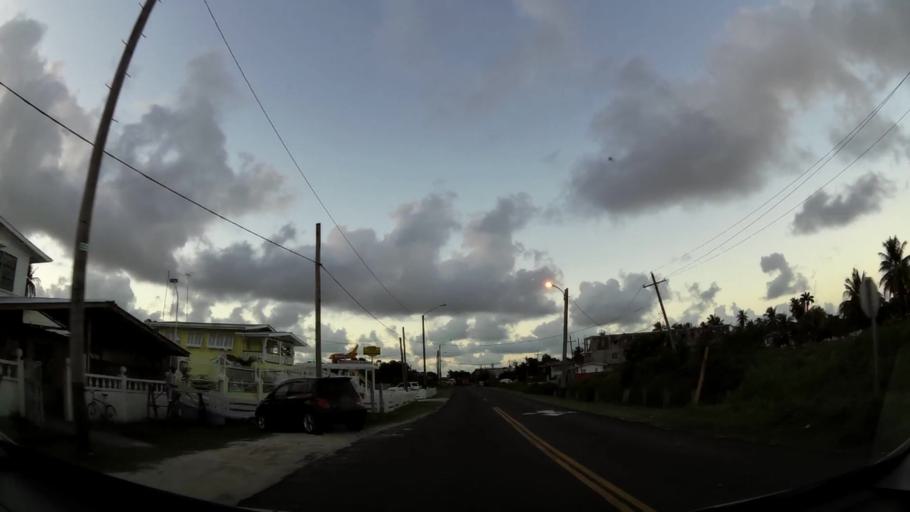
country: GY
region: Demerara-Mahaica
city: Georgetown
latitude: 6.8168
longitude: -58.0985
